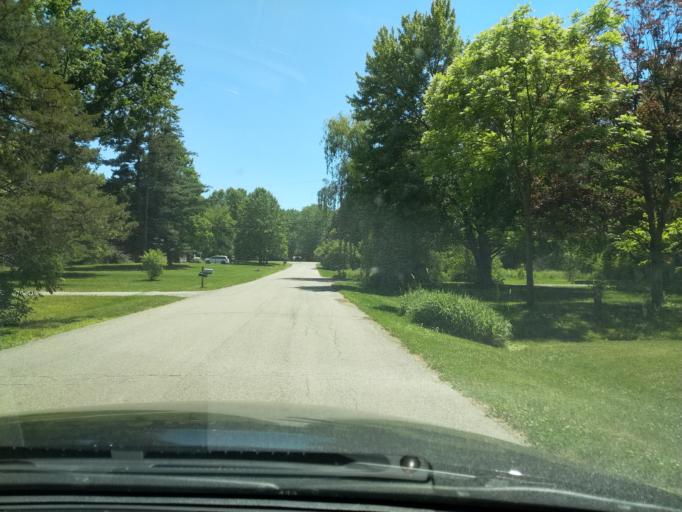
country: US
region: Indiana
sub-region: Hamilton County
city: Carmel
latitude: 39.9430
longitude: -86.1340
